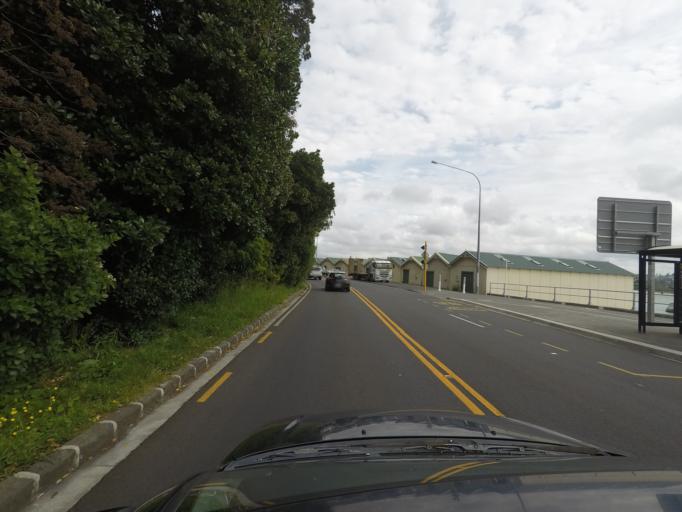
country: NZ
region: Auckland
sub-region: Auckland
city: Auckland
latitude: -36.8533
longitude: 174.8058
